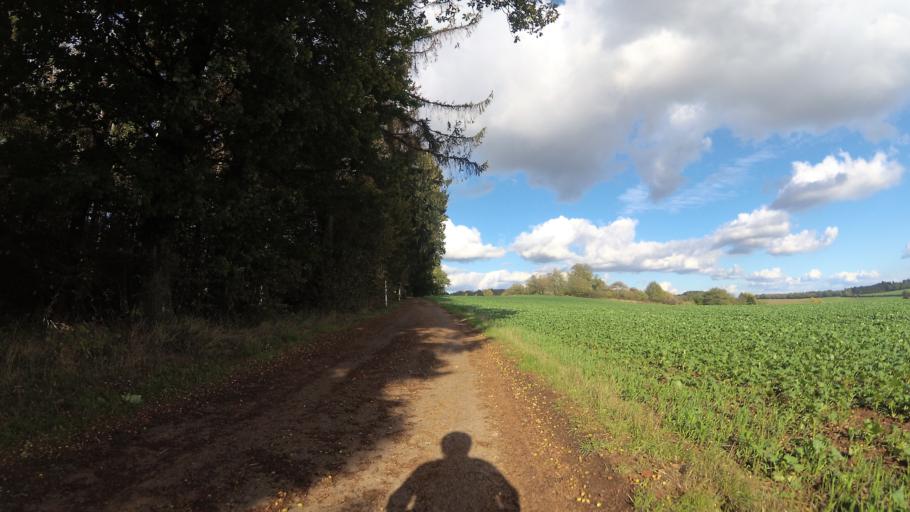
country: DE
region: Saarland
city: Marpingen
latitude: 49.4470
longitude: 7.0743
